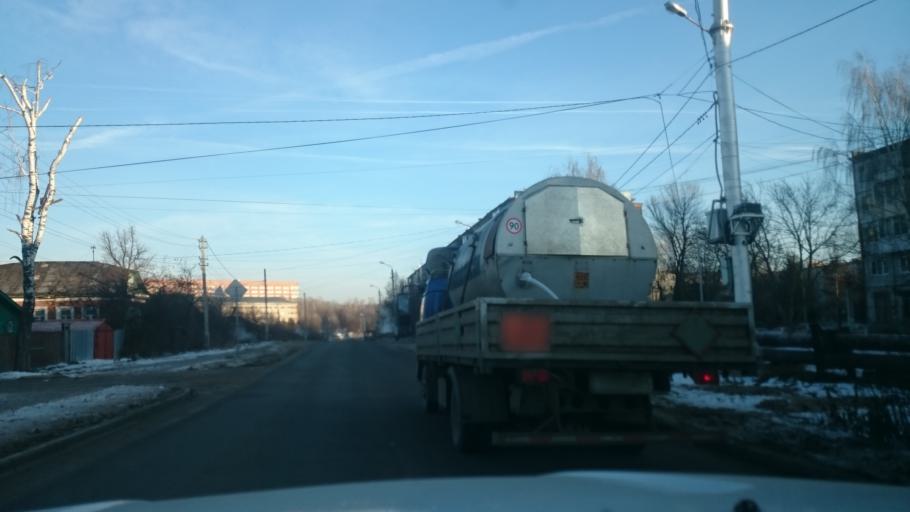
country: RU
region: Tula
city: Tula
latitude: 54.2046
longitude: 37.6958
